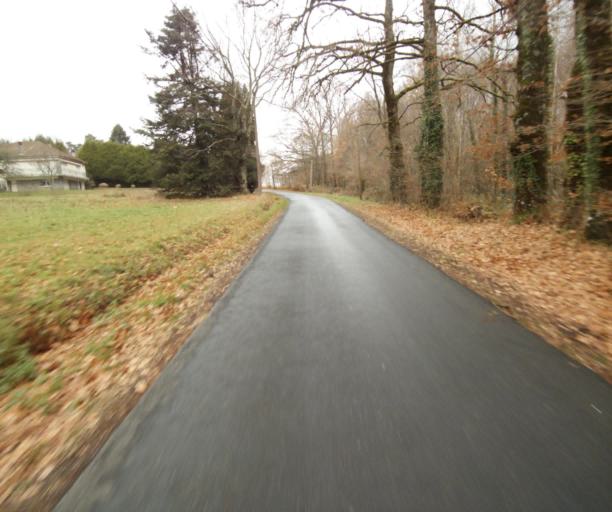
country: FR
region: Limousin
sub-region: Departement de la Correze
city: Saint-Mexant
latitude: 45.2782
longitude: 1.6349
